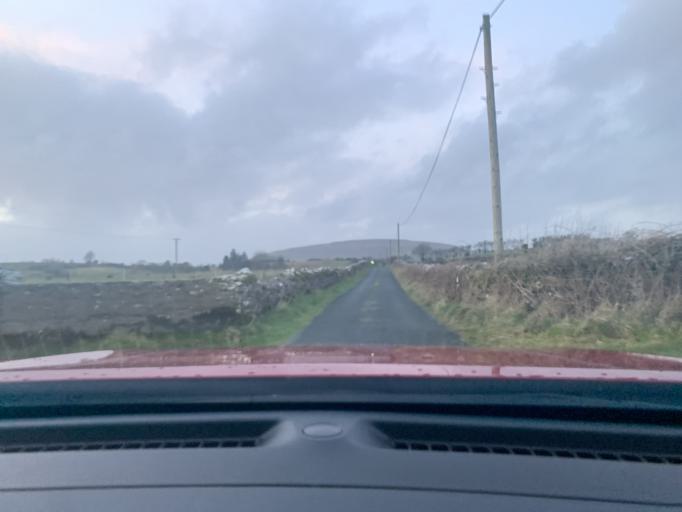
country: IE
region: Connaught
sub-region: Sligo
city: Ballymote
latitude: 54.0385
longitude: -8.4080
